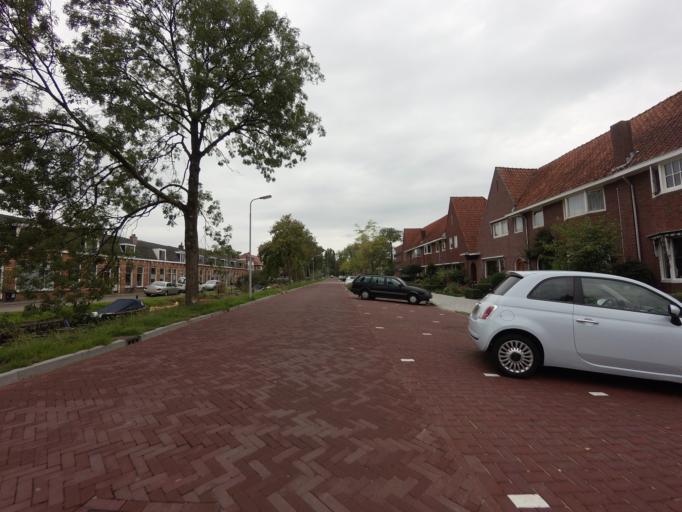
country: NL
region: Friesland
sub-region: Sudwest Fryslan
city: Sneek
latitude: 53.0363
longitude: 5.6575
